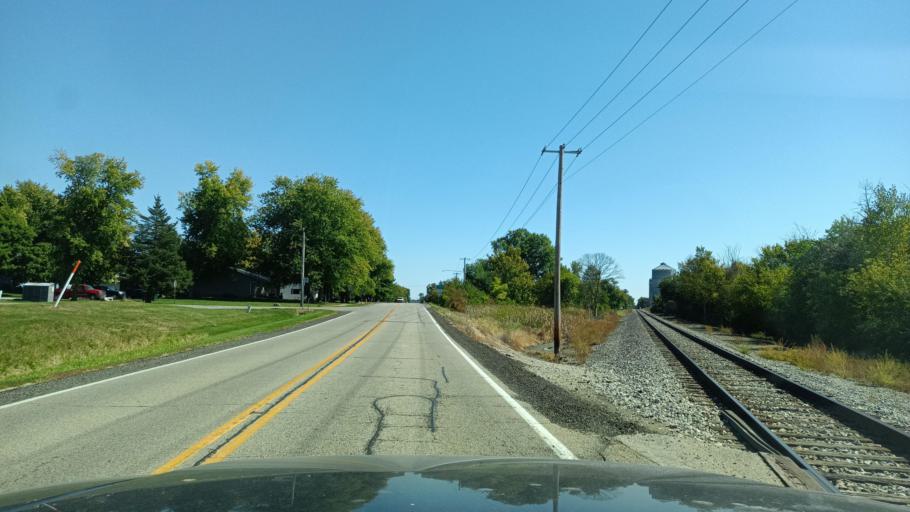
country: US
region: Illinois
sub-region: McLean County
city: Danvers
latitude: 40.6171
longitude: -89.2122
